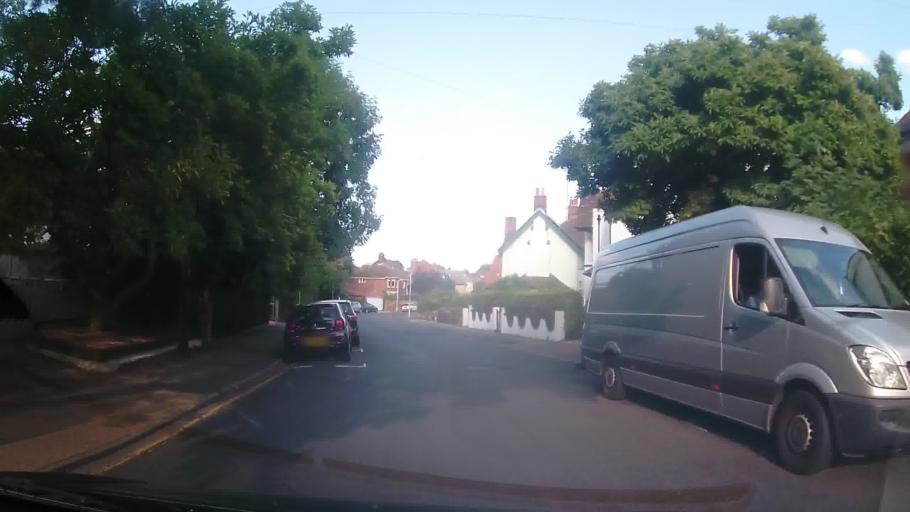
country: GB
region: England
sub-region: Kent
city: Canterbury
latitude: 51.2740
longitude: 1.0906
